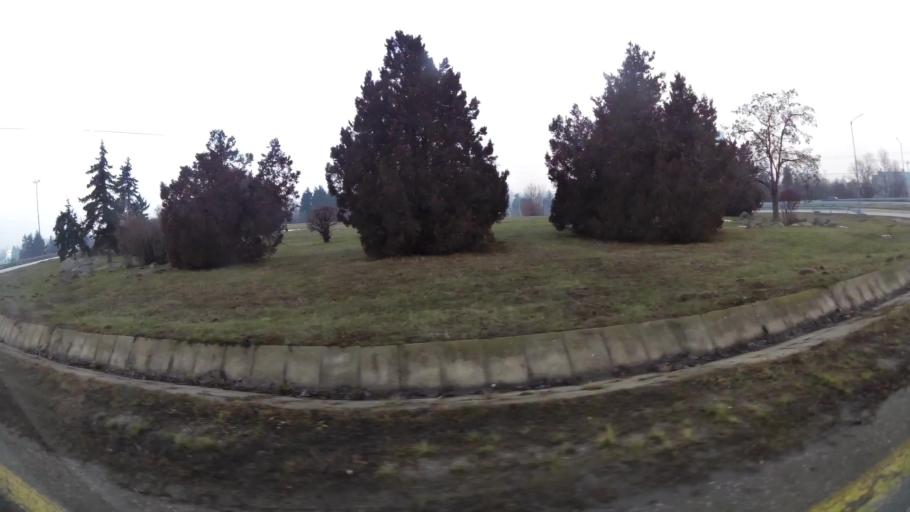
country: BG
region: Sofia-Capital
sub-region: Stolichna Obshtina
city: Sofia
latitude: 42.6530
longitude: 23.2857
